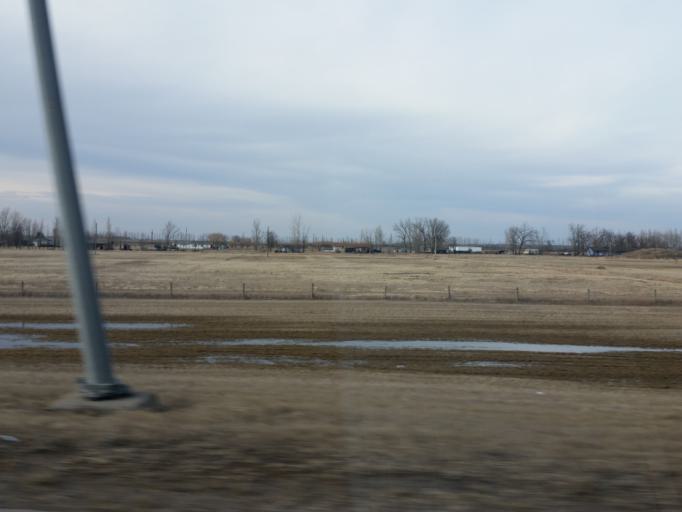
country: US
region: North Dakota
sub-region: Cass County
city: West Fargo
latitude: 46.8776
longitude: -96.9520
